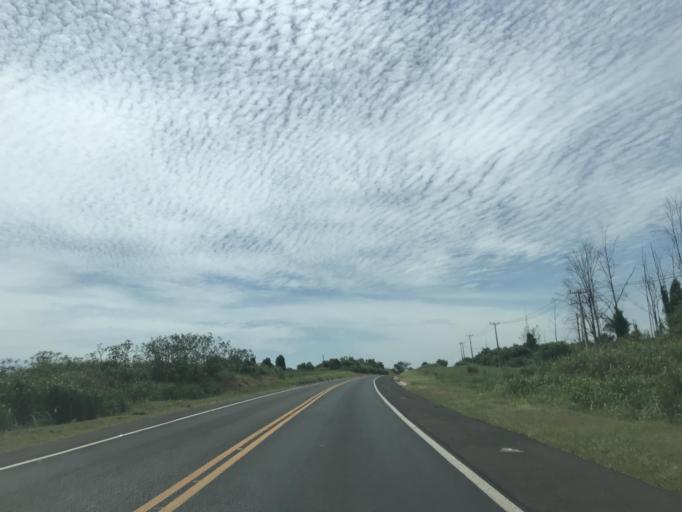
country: BR
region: Parana
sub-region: Paranavai
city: Paranavai
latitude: -23.0145
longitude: -52.5138
